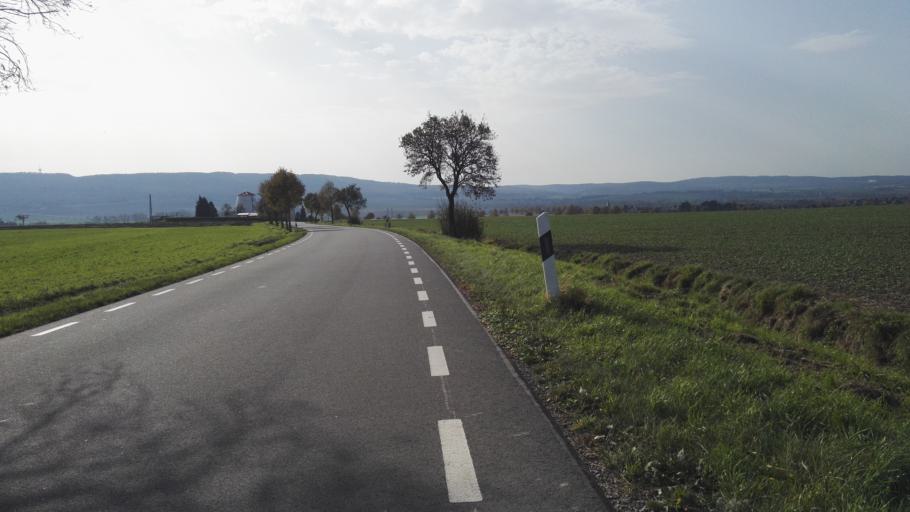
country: DE
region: Lower Saxony
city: Bad Salzdetfurth
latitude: 52.1148
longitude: 10.0177
